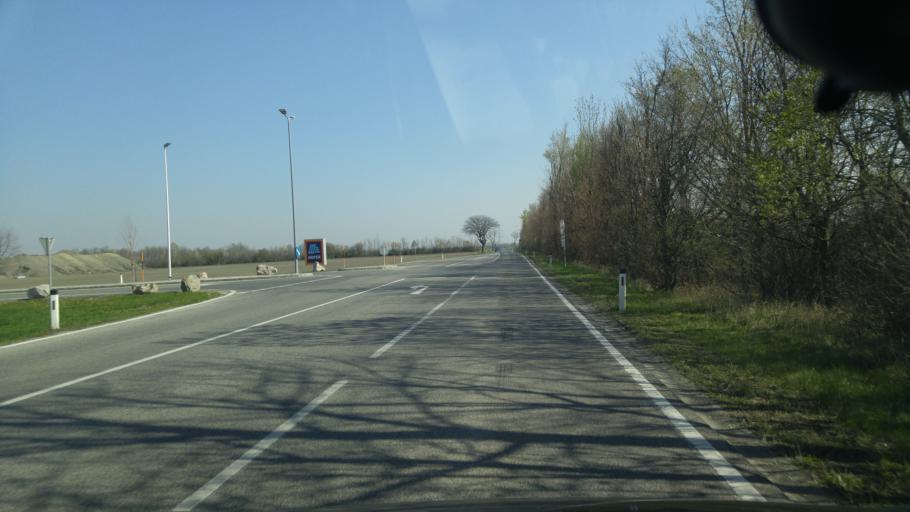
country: AT
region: Lower Austria
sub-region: Politischer Bezirk Baden
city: Trumau
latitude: 47.9955
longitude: 16.3659
